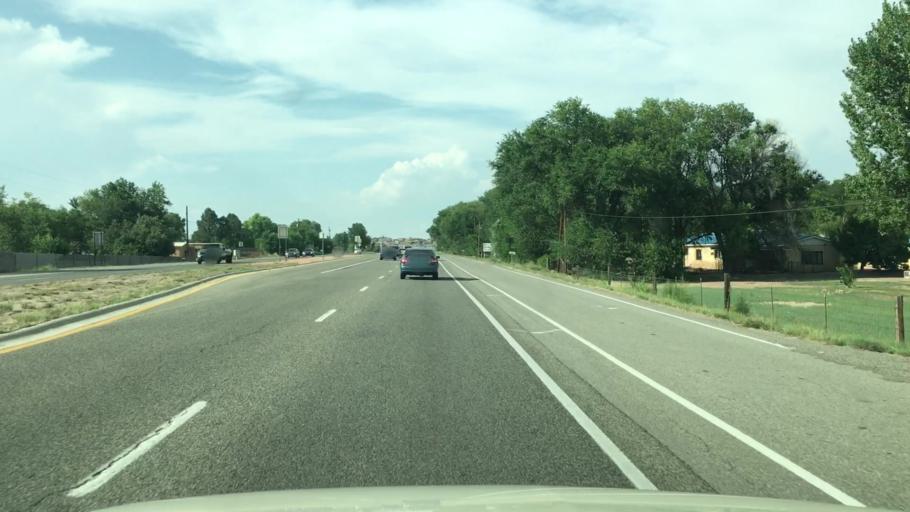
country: US
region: New Mexico
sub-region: Santa Fe County
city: Pojoaque
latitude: 35.9022
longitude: -106.0195
